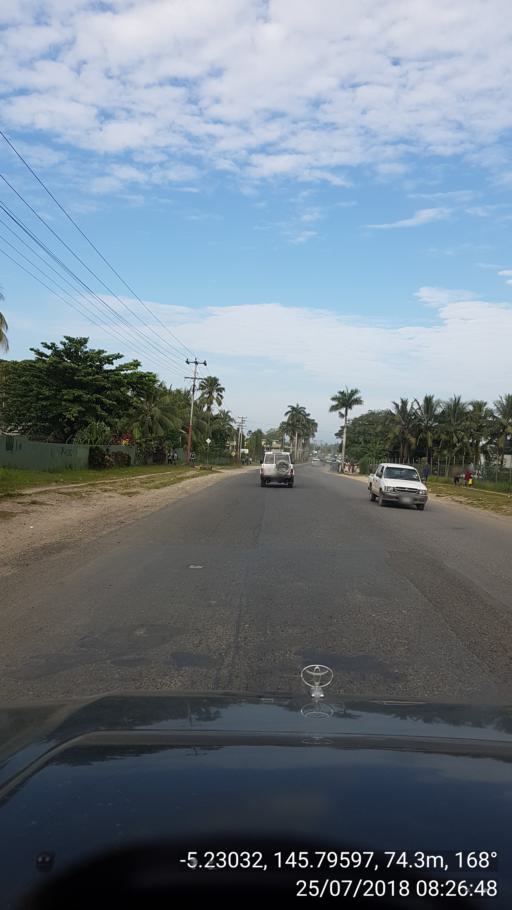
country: PG
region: Madang
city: Madang
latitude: -5.2303
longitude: 145.7961
